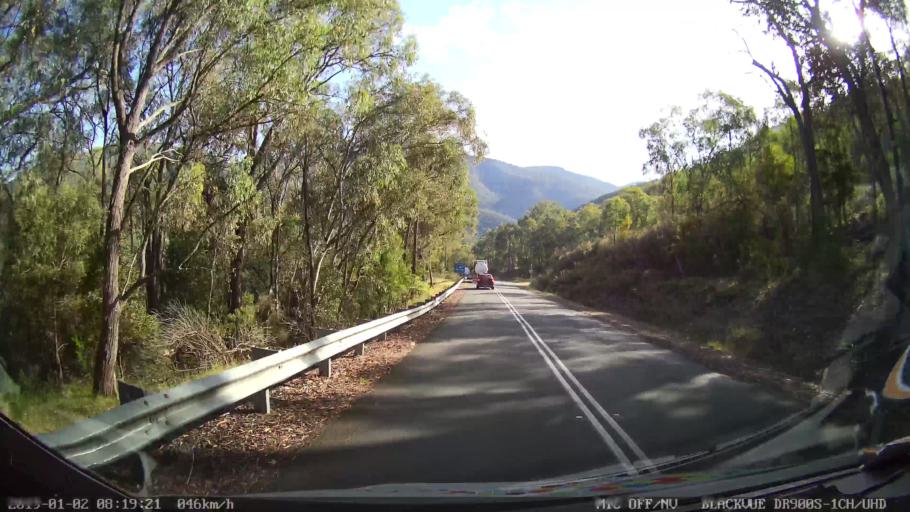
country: AU
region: New South Wales
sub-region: Tumut Shire
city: Tumut
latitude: -35.5755
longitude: 148.3210
